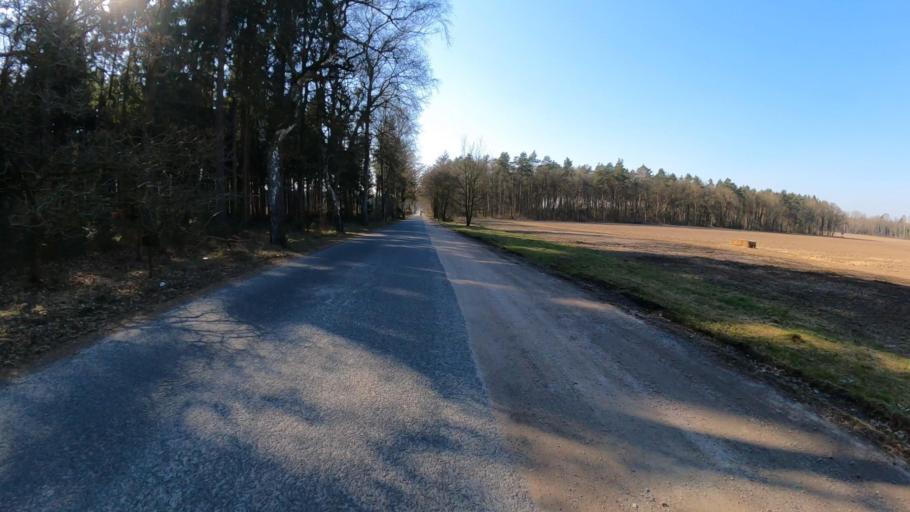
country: DE
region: Lower Saxony
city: Buchholz in der Nordheide
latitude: 53.3100
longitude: 9.8371
